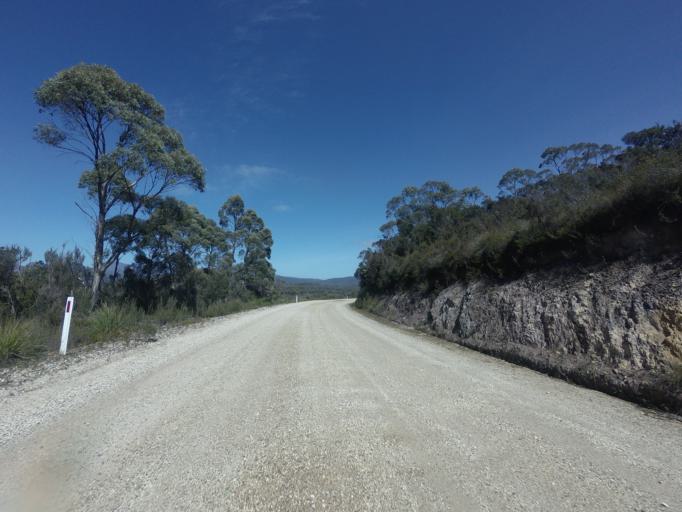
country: AU
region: Tasmania
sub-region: Huon Valley
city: Geeveston
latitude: -43.0371
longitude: 146.3322
